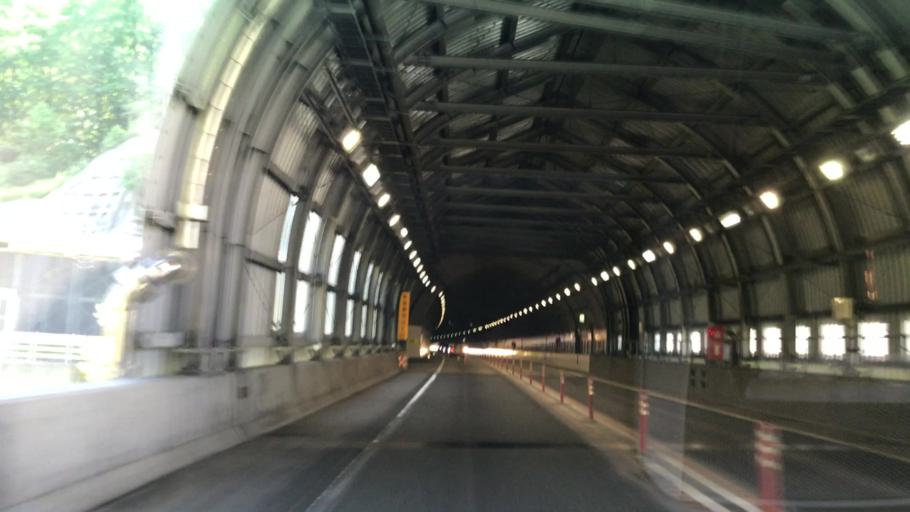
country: JP
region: Hokkaido
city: Iwamizawa
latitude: 42.9325
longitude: 142.1103
